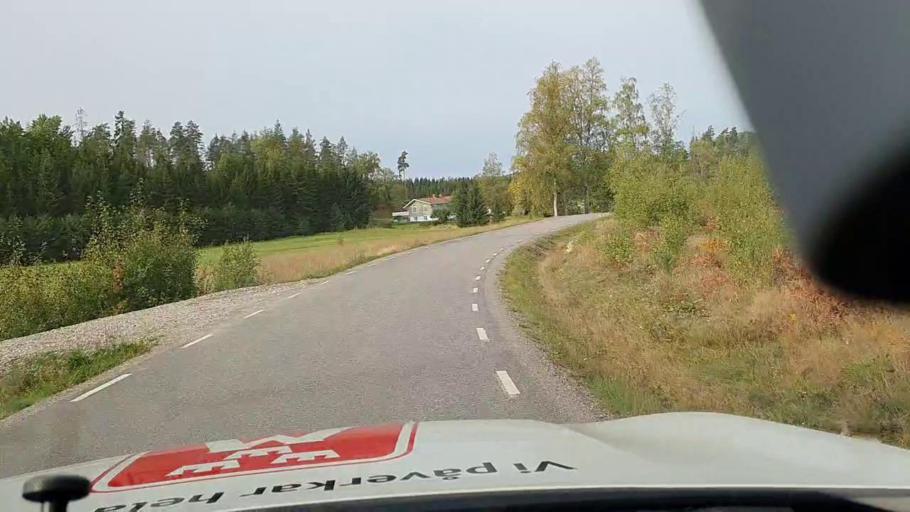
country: SE
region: Soedermanland
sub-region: Nykopings Kommun
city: Nykoping
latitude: 58.8547
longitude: 16.9632
